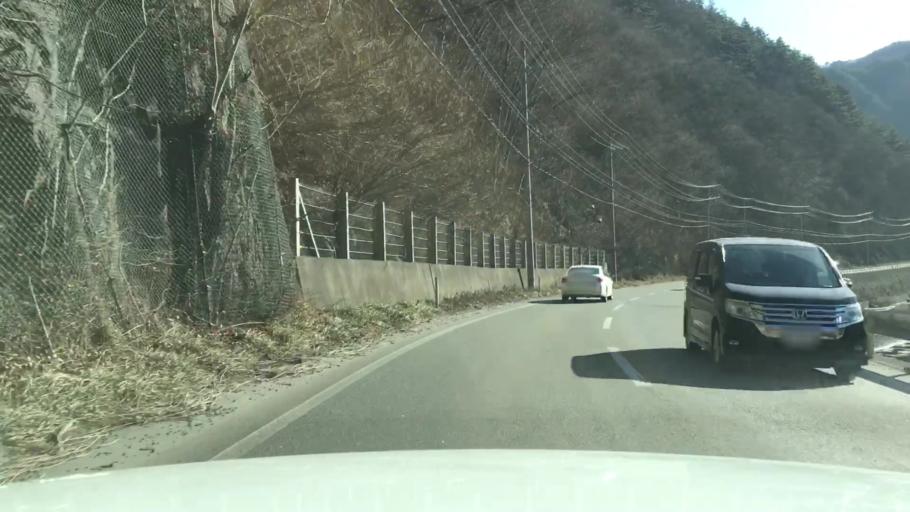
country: JP
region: Iwate
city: Miyako
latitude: 39.6187
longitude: 141.7935
